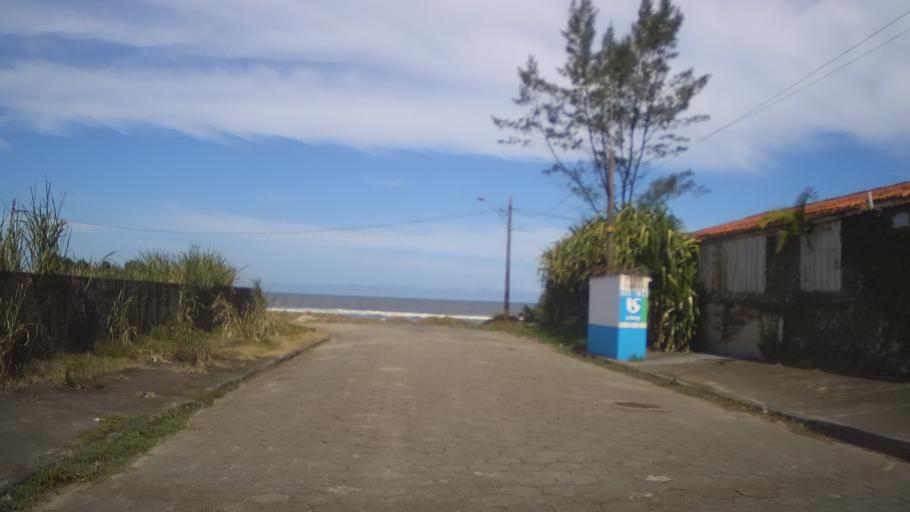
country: BR
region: Sao Paulo
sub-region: Itanhaem
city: Itanhaem
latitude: -24.1793
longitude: -46.7755
